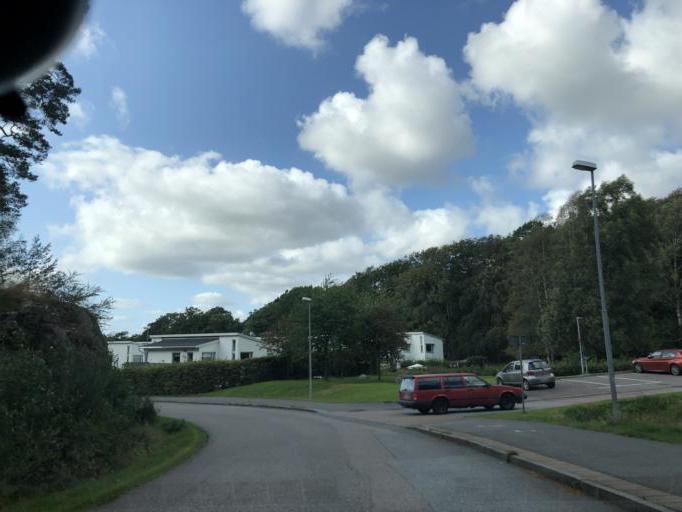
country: SE
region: Vaestra Goetaland
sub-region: Goteborg
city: Goeteborg
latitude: 57.7472
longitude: 11.9584
